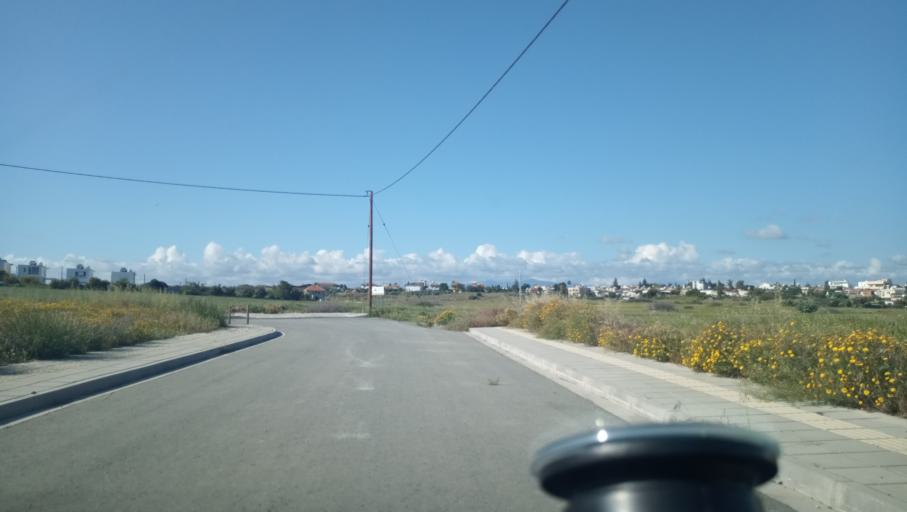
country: CY
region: Lefkosia
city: Geri
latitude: 35.1034
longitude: 33.3976
